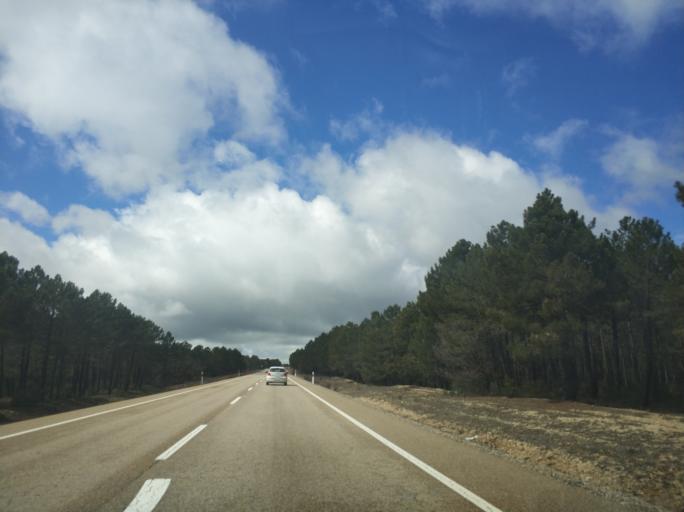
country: ES
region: Castille and Leon
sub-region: Provincia de Soria
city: Muriel Viejo
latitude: 41.8158
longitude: -2.9127
